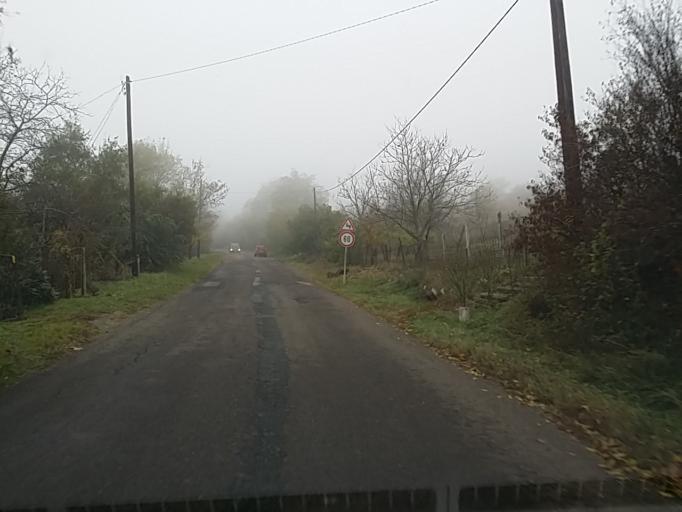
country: HU
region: Heves
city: Gyongyossolymos
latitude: 47.8108
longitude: 19.9646
